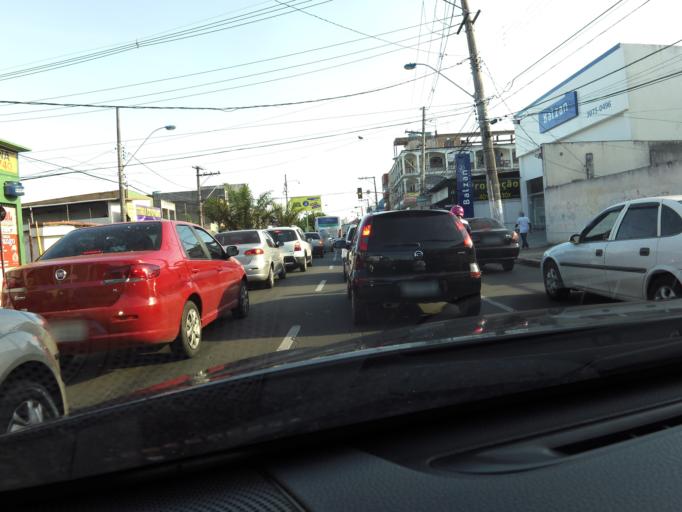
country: BR
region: Espirito Santo
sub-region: Vila Velha
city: Vila Velha
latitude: -20.3475
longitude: -40.2937
